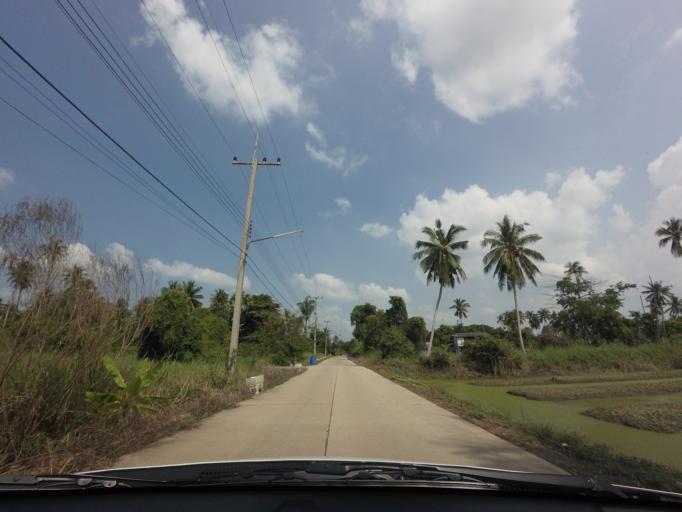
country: TH
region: Nakhon Pathom
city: Nakhon Chai Si
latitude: 13.8131
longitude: 100.1907
